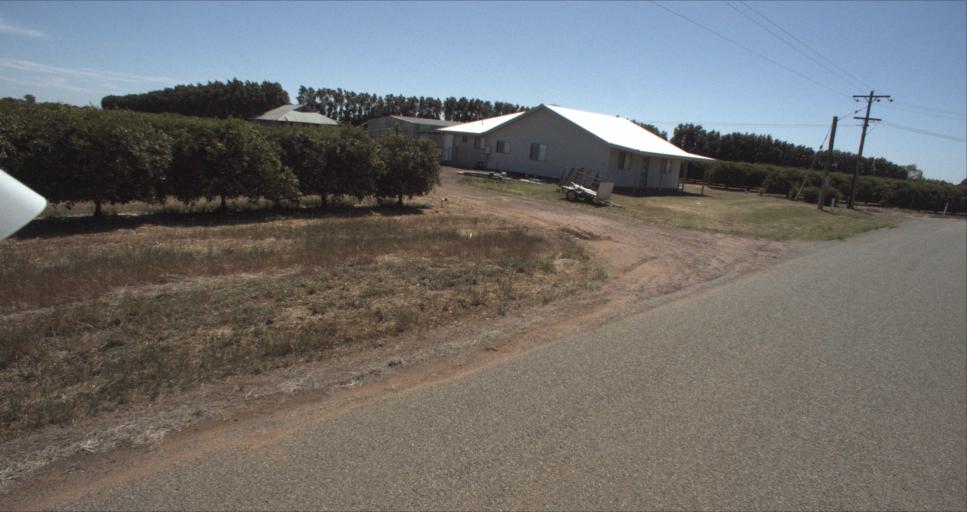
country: AU
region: New South Wales
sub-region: Leeton
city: Leeton
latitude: -34.5392
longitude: 146.3521
